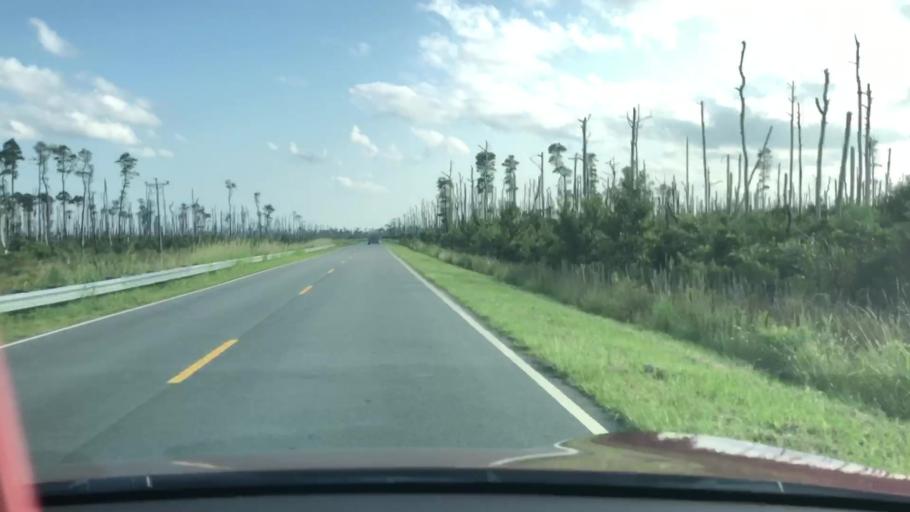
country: US
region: North Carolina
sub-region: Dare County
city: Wanchese
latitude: 35.6391
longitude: -75.7786
